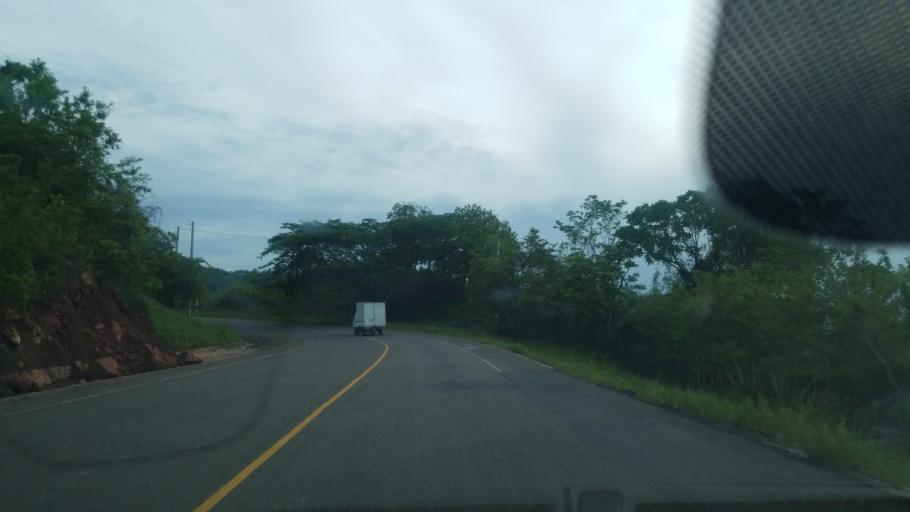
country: HN
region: Santa Barbara
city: Concepcion del Sur
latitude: 14.8108
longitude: -88.1802
